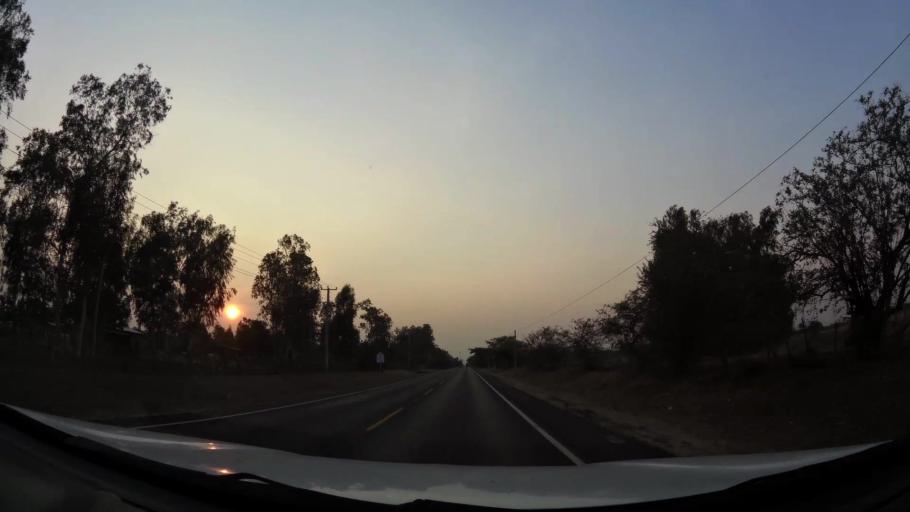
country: NI
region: Leon
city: La Paz Centro
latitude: 12.3262
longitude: -86.8008
